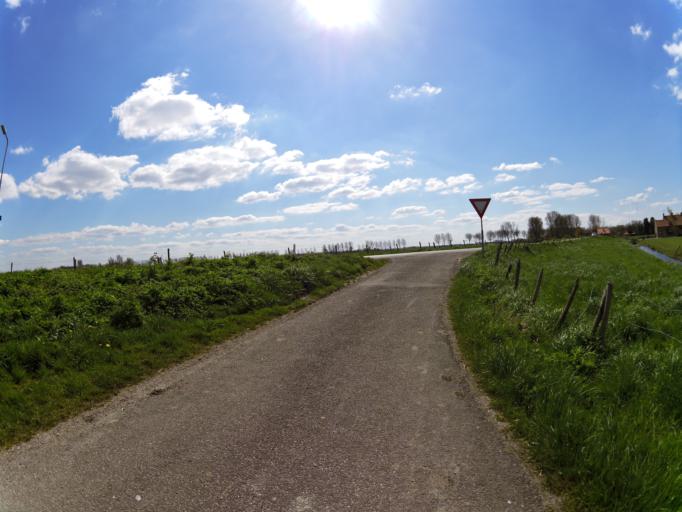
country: NL
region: South Holland
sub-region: Gemeente Hellevoetsluis
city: Nieuw-Helvoet
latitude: 51.8758
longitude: 4.0981
